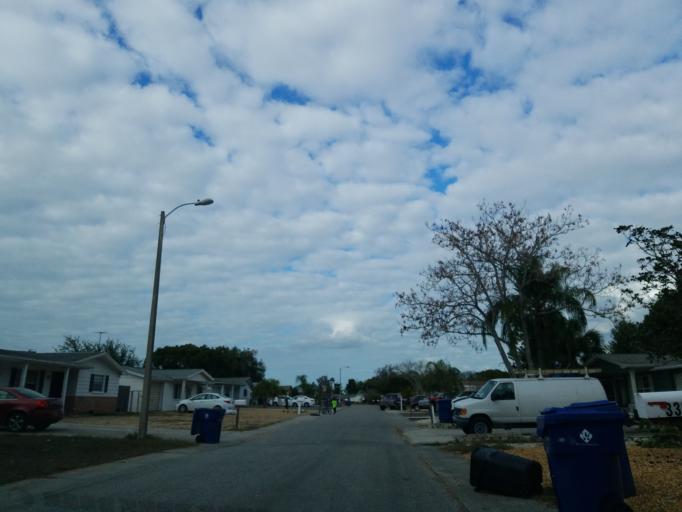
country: US
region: Florida
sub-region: Pasco County
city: Beacon Square
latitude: 28.2066
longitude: -82.7602
